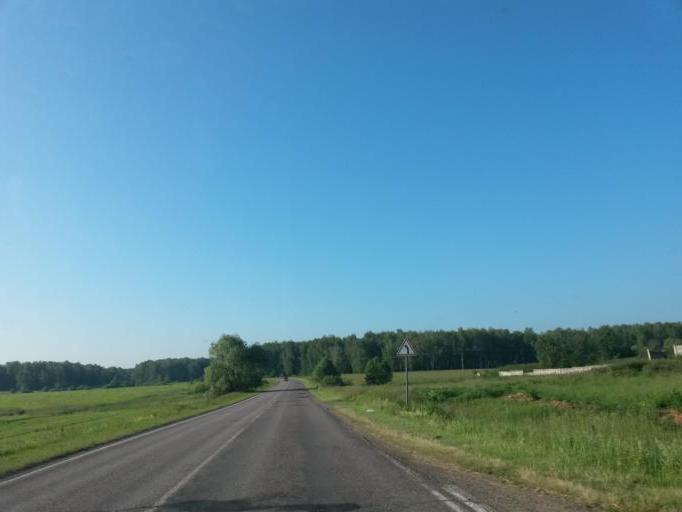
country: RU
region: Moskovskaya
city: Lyubuchany
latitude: 55.2366
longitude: 37.6434
